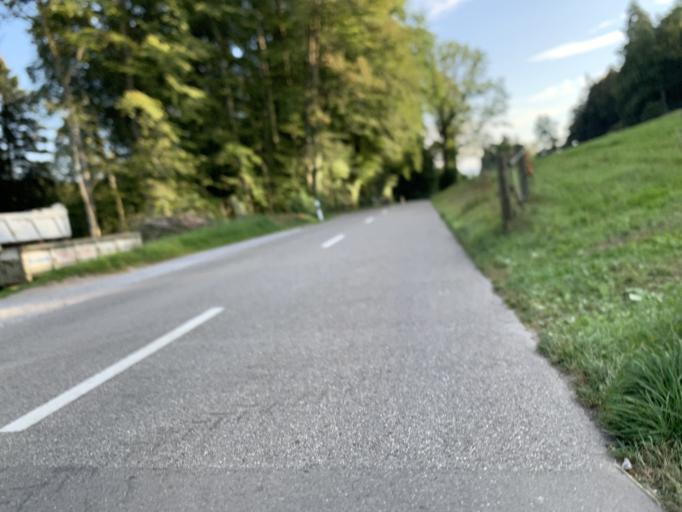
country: CH
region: Zurich
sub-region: Bezirk Hinwil
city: Hinwil
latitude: 47.3111
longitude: 8.8530
